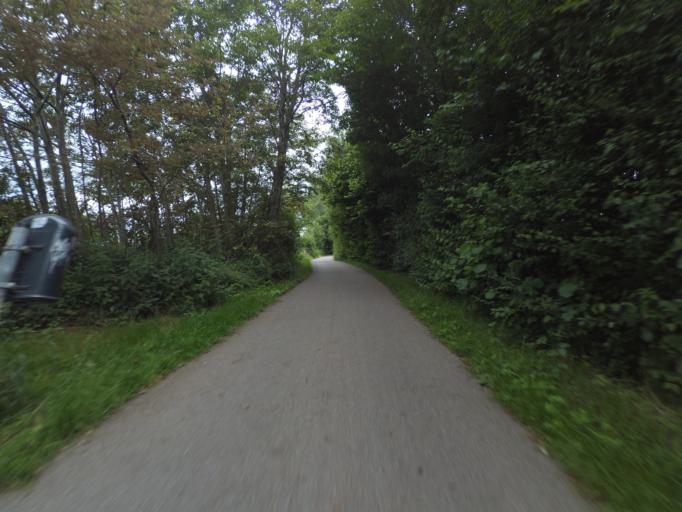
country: DE
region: North Rhine-Westphalia
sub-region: Regierungsbezirk Koln
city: Wurselen
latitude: 50.7698
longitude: 6.1501
